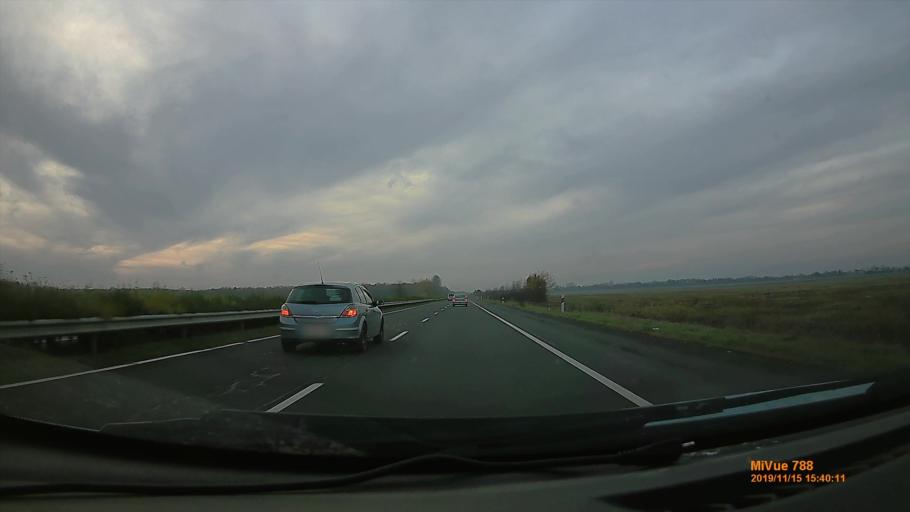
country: HU
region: Bekes
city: Bekescsaba
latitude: 46.6741
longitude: 21.1572
